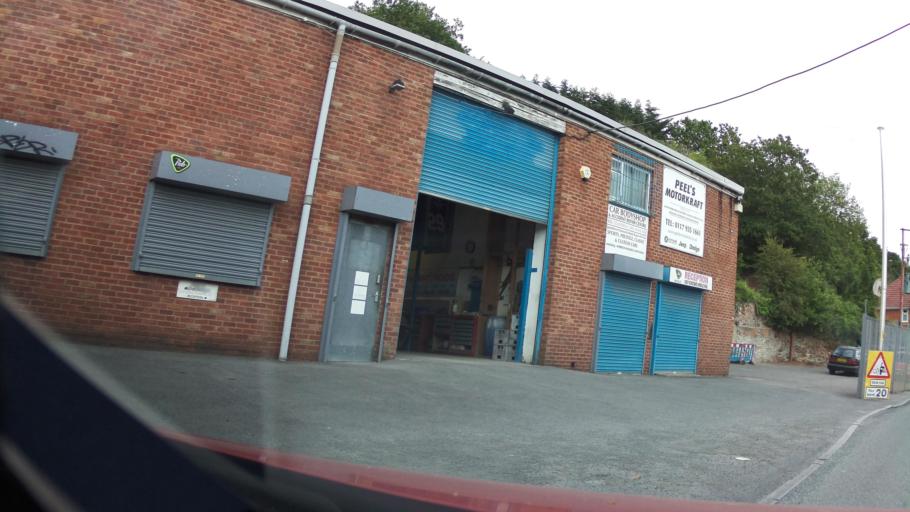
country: GB
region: England
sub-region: South Gloucestershire
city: Kingswood
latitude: 51.4561
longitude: -2.5431
